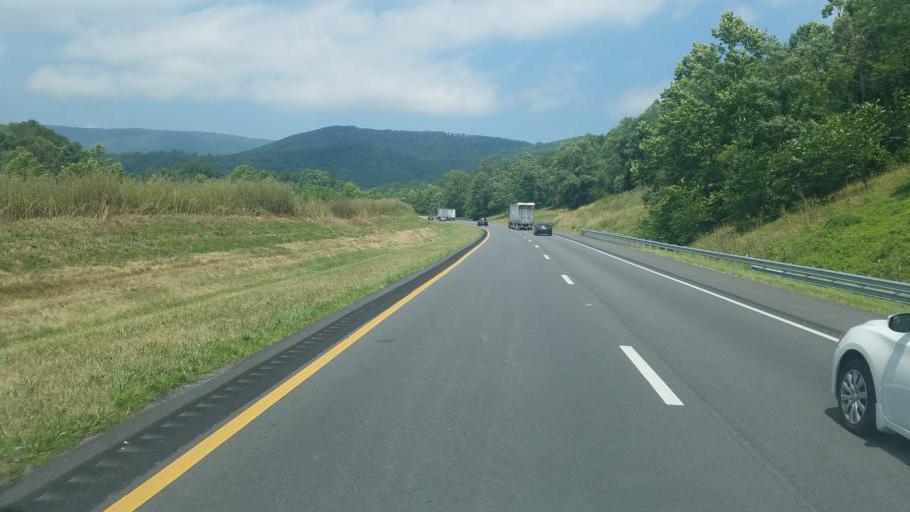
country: US
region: West Virginia
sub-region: Mercer County
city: Bluefield
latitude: 37.2330
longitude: -81.0956
